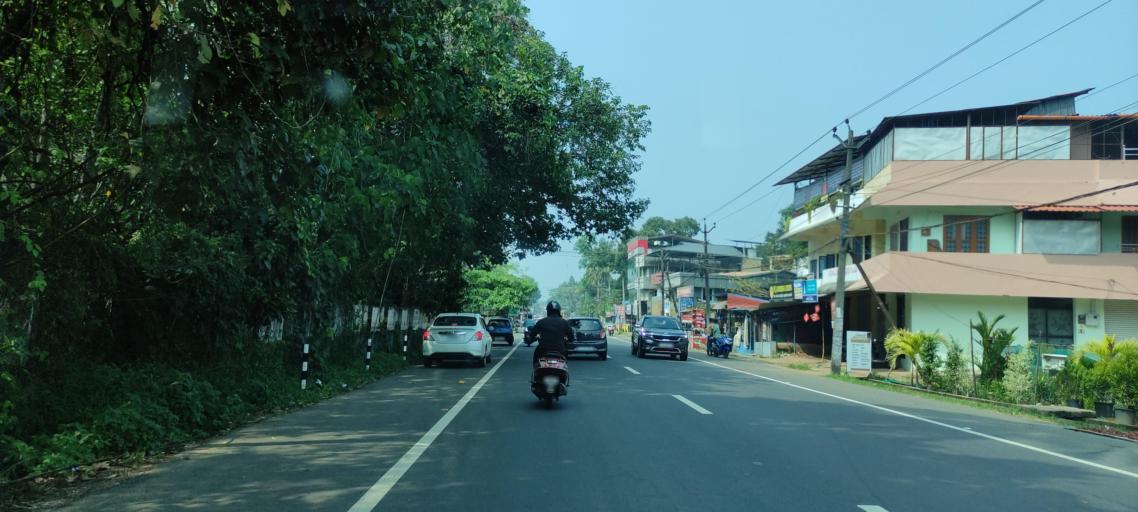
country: IN
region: Kerala
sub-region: Pattanamtitta
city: Adur
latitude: 9.2126
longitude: 76.6844
